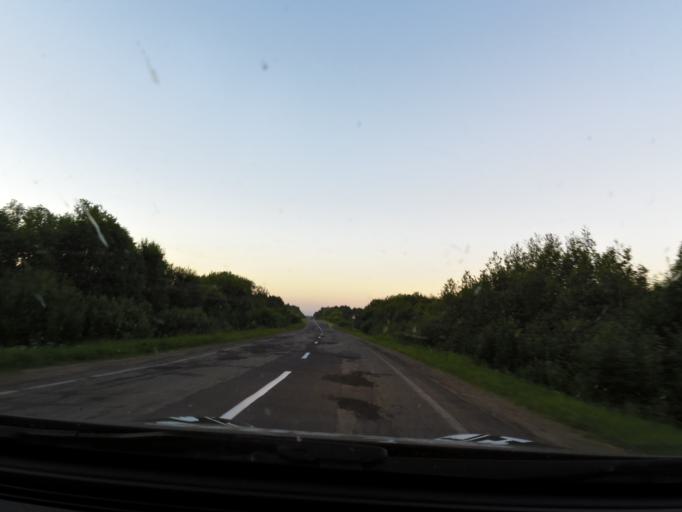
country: RU
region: Jaroslavl
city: Lyubim
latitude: 58.3259
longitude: 41.0486
